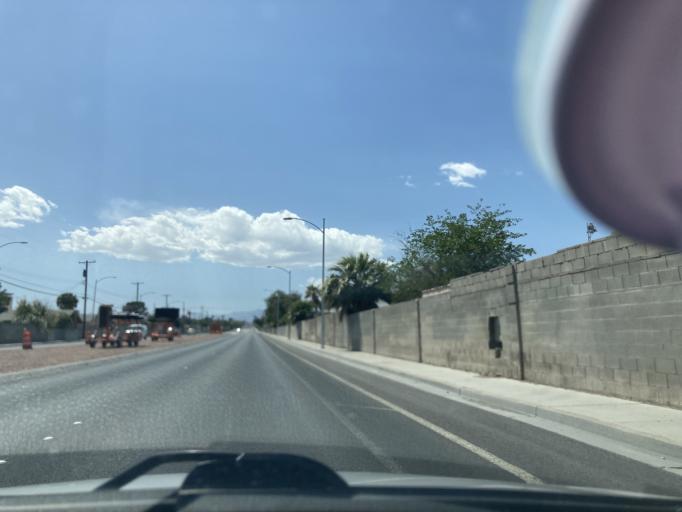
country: US
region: Nevada
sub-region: Clark County
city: North Las Vegas
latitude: 36.1813
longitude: -115.1178
